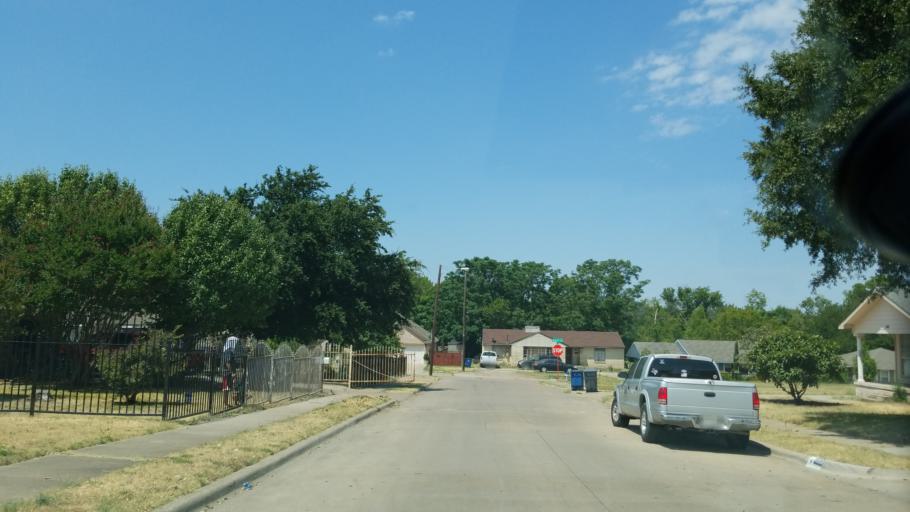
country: US
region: Texas
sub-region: Dallas County
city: Cockrell Hill
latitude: 32.7305
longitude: -96.8971
